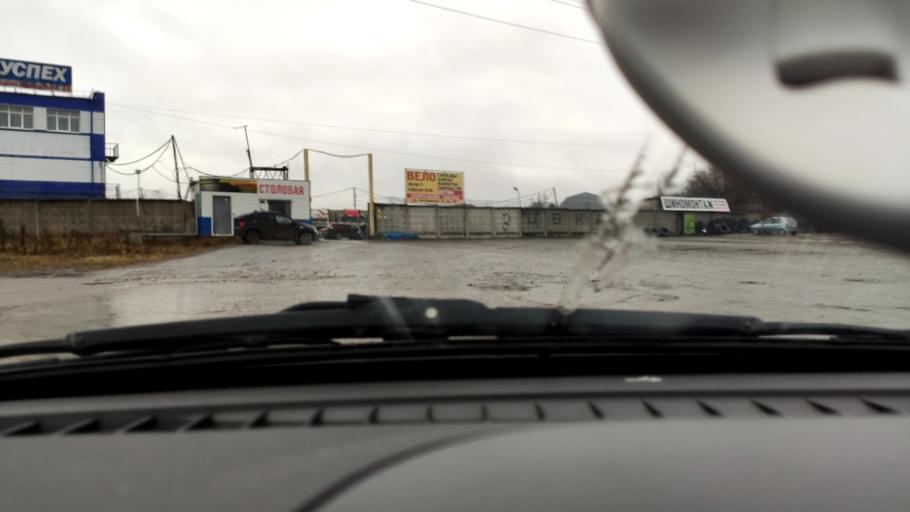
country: RU
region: Perm
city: Froly
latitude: 57.9702
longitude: 56.2875
